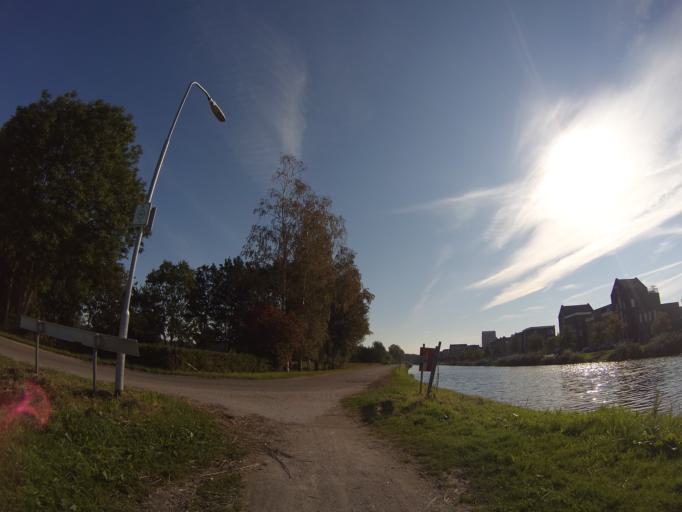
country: NL
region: Gelderland
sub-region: Gemeente Nijkerk
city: Nijkerk
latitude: 52.2024
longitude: 5.4298
